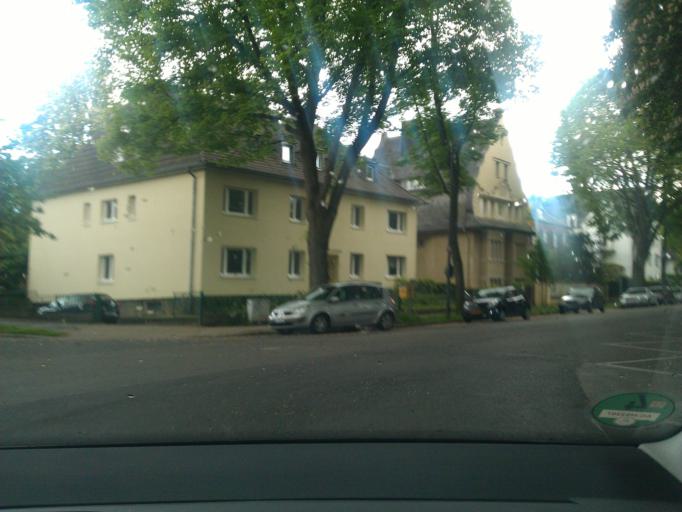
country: DE
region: North Rhine-Westphalia
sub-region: Regierungsbezirk Koln
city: Aachen
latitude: 50.7593
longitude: 6.0753
